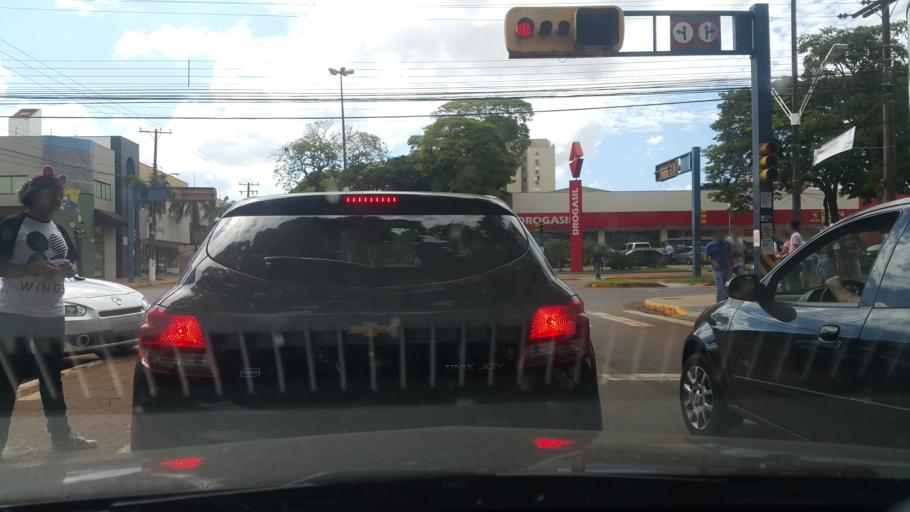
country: BR
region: Mato Grosso do Sul
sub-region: Dourados
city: Dourados
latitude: -22.2270
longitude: -54.8119
